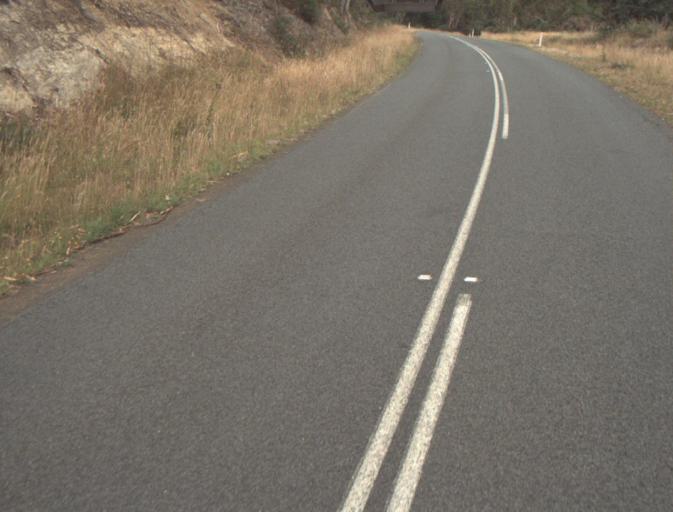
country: AU
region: Tasmania
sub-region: Northern Midlands
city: Evandale
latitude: -41.4900
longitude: 147.5019
